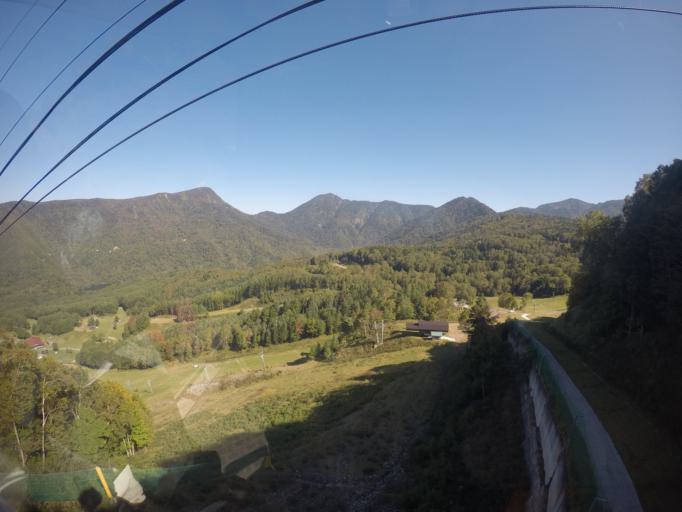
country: JP
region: Tochigi
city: Nikko
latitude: 36.8106
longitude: 139.3425
